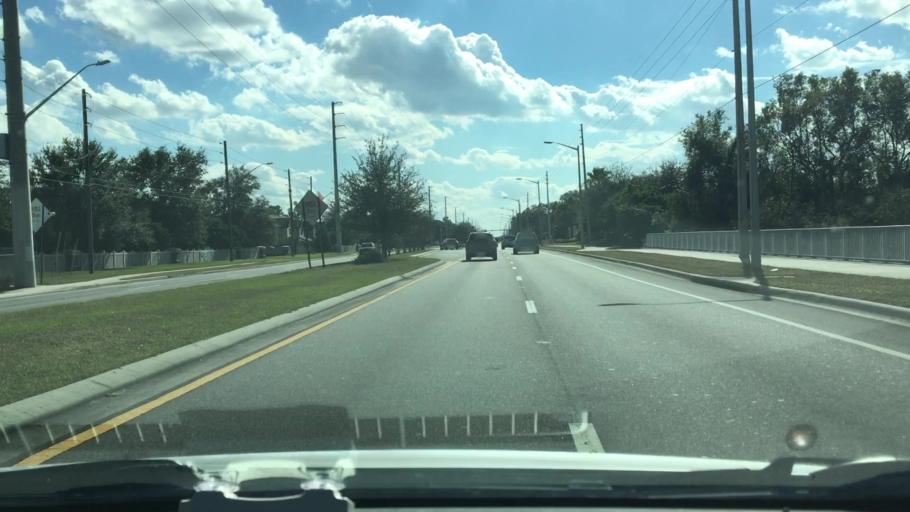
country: US
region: Florida
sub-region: Orange County
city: Conway
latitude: 28.4772
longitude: -81.3308
